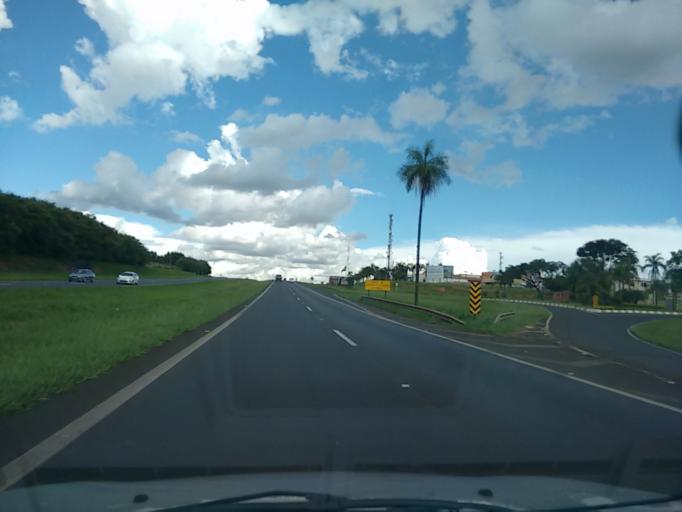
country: BR
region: Sao Paulo
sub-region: Ibate
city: Ibate
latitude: -21.9480
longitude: -47.9965
